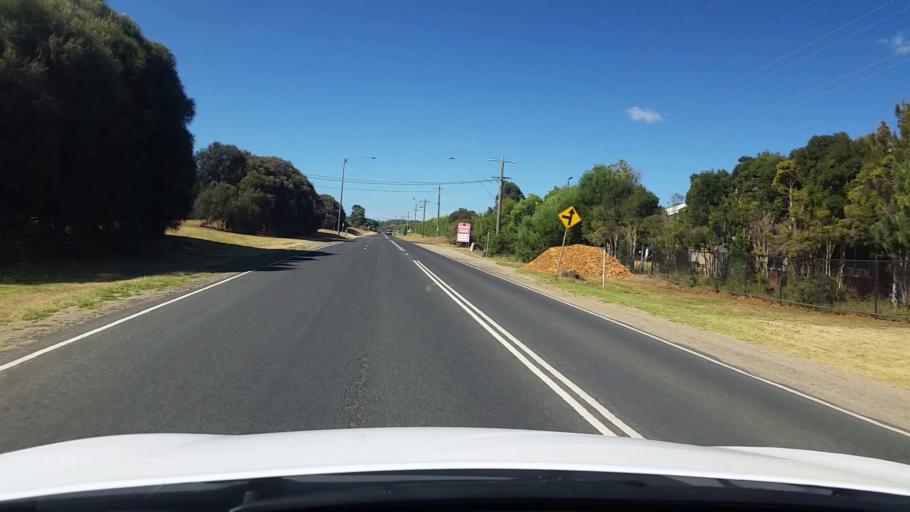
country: AU
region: Victoria
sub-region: Mornington Peninsula
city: Rosebud West
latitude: -38.4114
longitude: 144.8875
